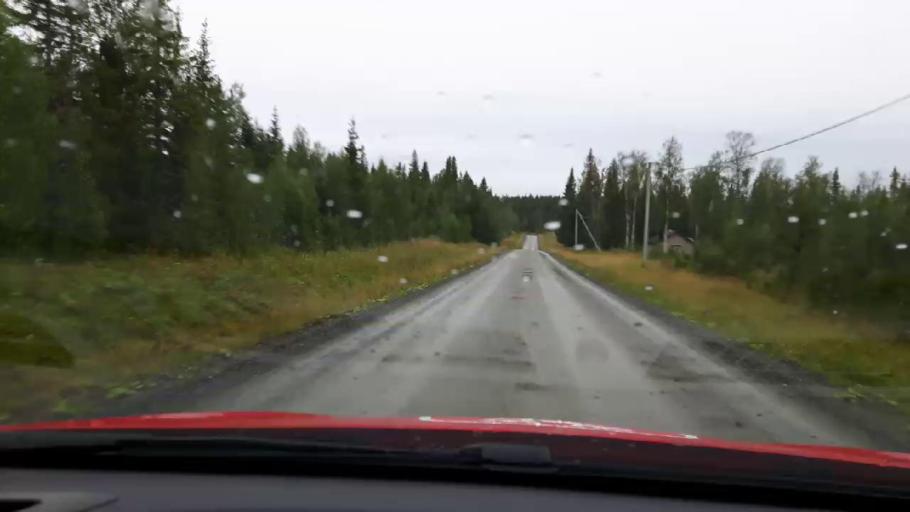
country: SE
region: Jaemtland
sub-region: Are Kommun
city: Are
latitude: 63.4382
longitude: 12.8074
